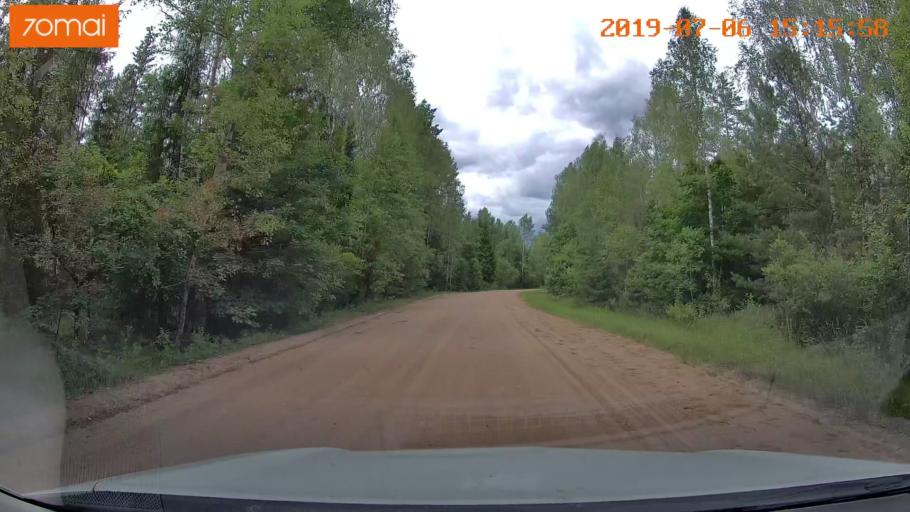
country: BY
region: Minsk
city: Ivyanyets
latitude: 53.9774
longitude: 26.6816
